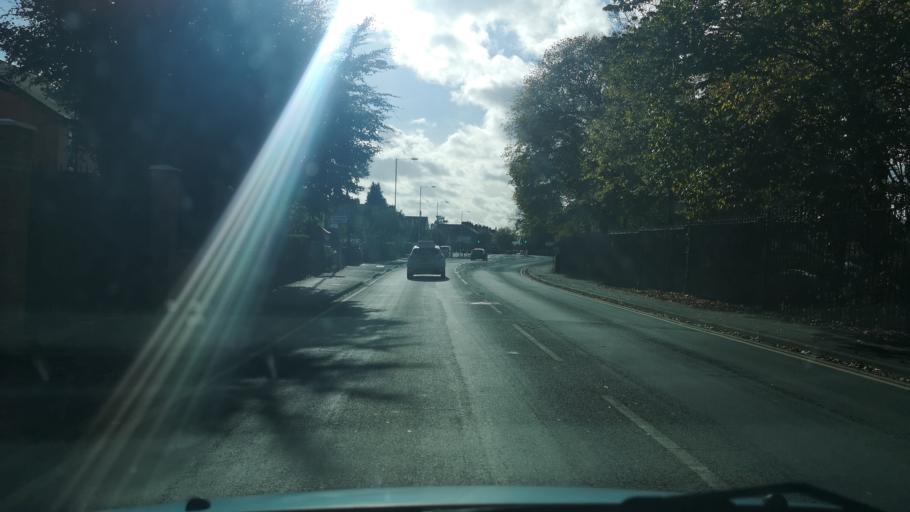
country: GB
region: England
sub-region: City and Borough of Wakefield
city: Wakefield
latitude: 53.6924
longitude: -1.4854
